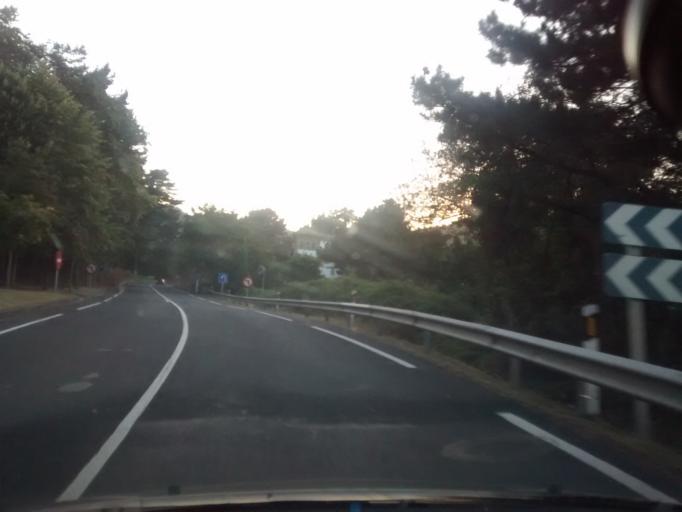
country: ES
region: Basque Country
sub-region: Provincia de Guipuzcoa
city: Mutriku
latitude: 43.3078
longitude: -2.3760
